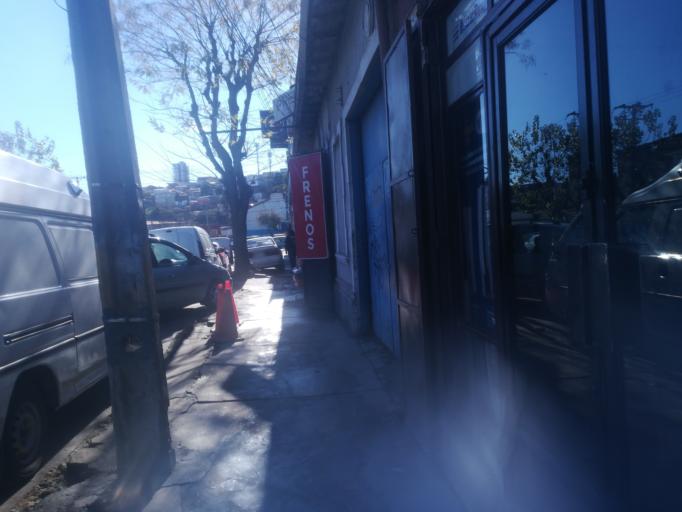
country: CL
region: Valparaiso
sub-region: Provincia de Valparaiso
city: Vina del Mar
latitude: -33.0108
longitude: -71.5417
